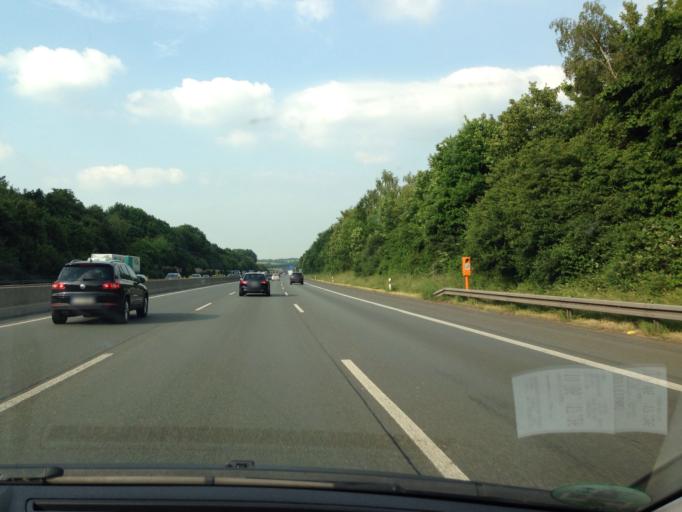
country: DE
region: North Rhine-Westphalia
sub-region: Regierungsbezirk Arnsberg
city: Holzwickede
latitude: 51.4915
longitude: 7.6304
